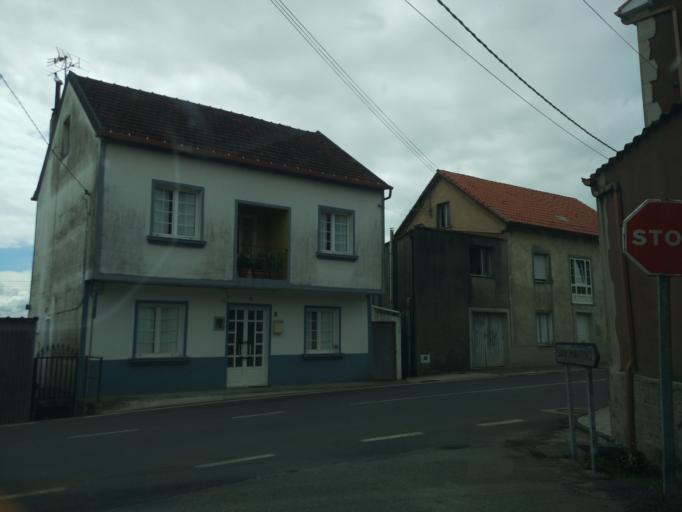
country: ES
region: Galicia
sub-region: Provincia da Coruna
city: Boiro
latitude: 42.6480
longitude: -8.8605
